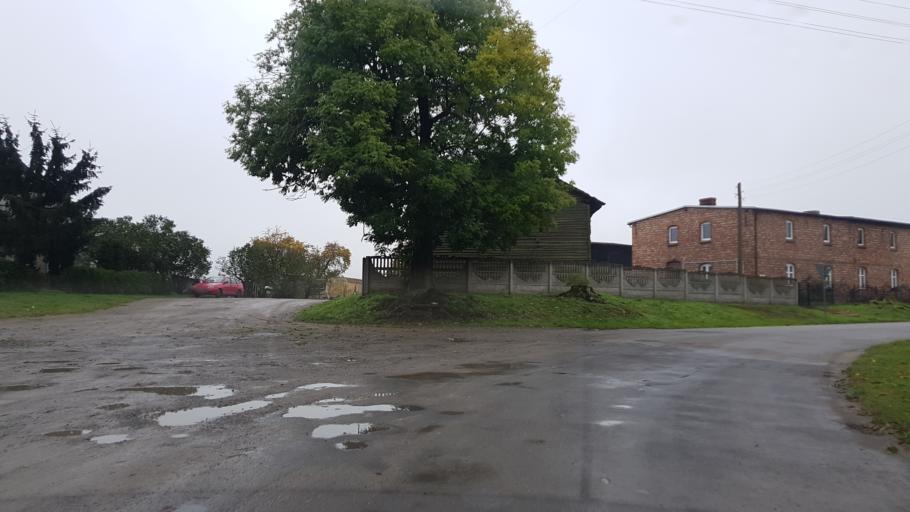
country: PL
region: West Pomeranian Voivodeship
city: Trzcinsko Zdroj
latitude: 53.0577
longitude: 14.5350
